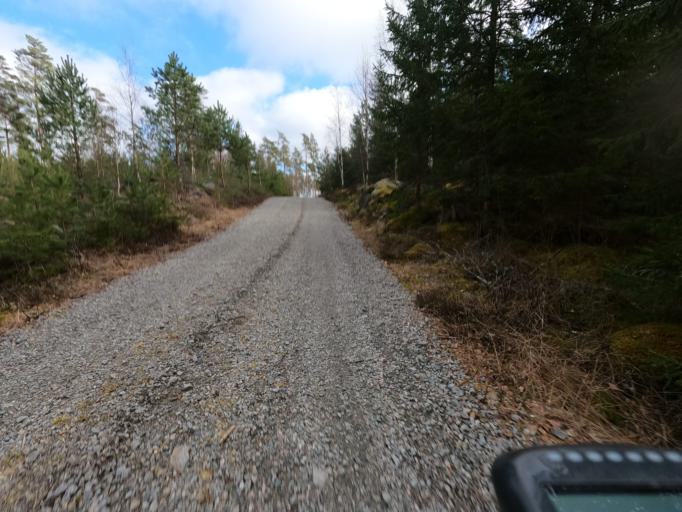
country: SE
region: Kronoberg
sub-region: Alvesta Kommun
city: Vislanda
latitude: 56.8141
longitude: 14.3823
